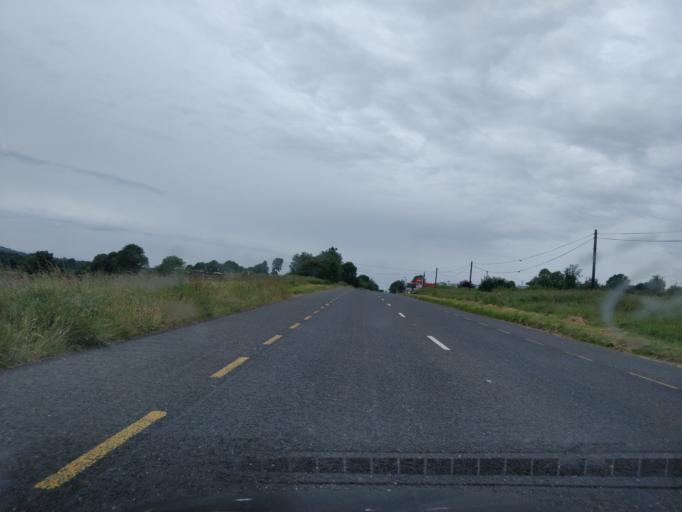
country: IE
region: Munster
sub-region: North Tipperary
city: Roscrea
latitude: 52.9597
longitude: -7.7170
